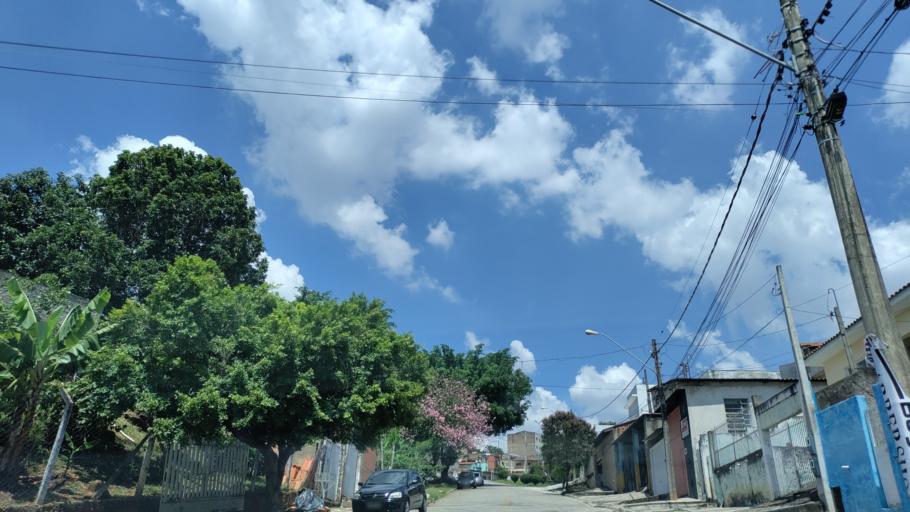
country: BR
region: Sao Paulo
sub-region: Sorocaba
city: Sorocaba
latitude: -23.4847
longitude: -47.4625
